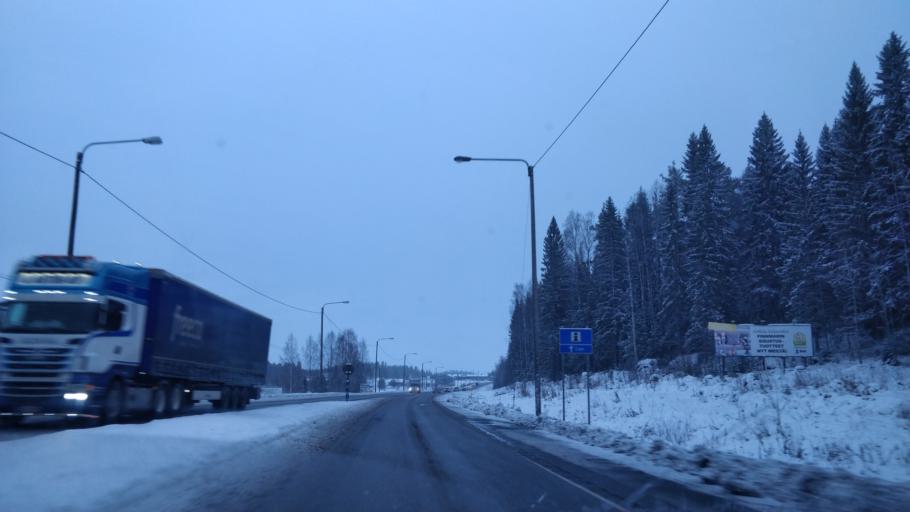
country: FI
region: Central Finland
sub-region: Saarijaervi-Viitasaari
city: Viitasaari
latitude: 63.0945
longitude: 25.8516
